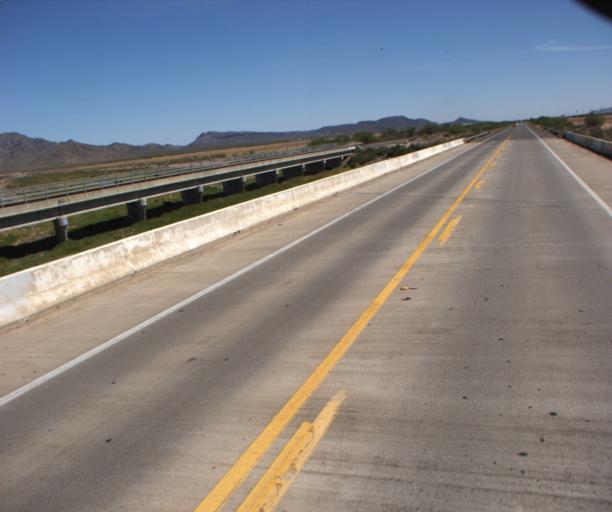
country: US
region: Arizona
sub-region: Maricopa County
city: Sun Lakes
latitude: 33.1682
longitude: -111.7907
